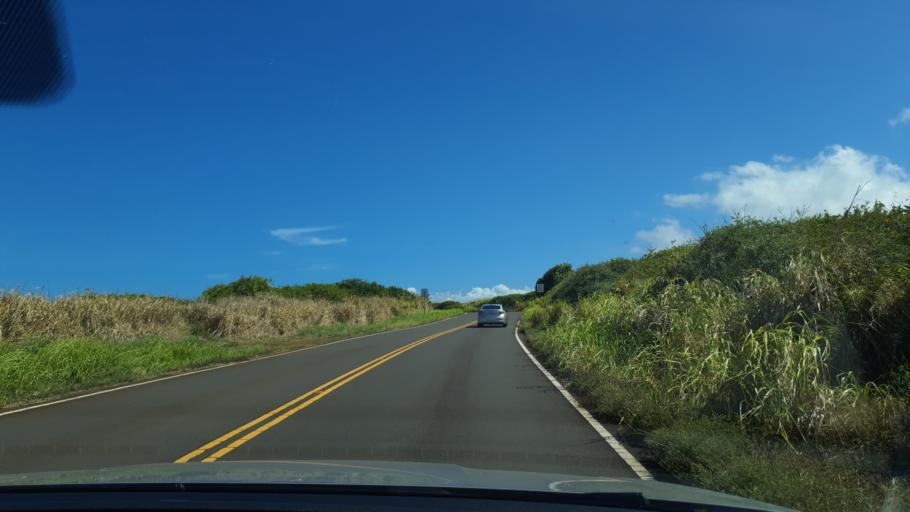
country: US
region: Hawaii
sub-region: Maui County
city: Napili-Honokowai
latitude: 21.0151
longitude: -156.5744
